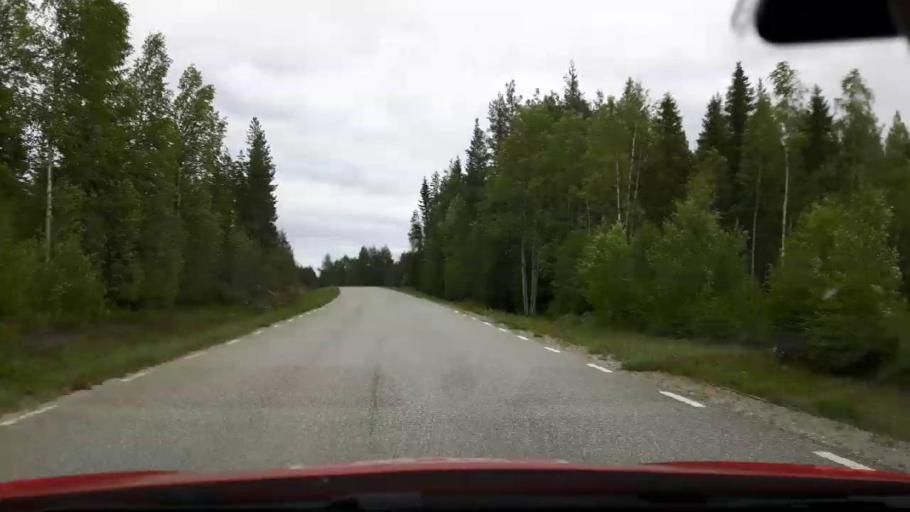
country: SE
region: Jaemtland
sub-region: Ragunda Kommun
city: Hammarstrand
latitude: 63.2097
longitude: 16.0080
